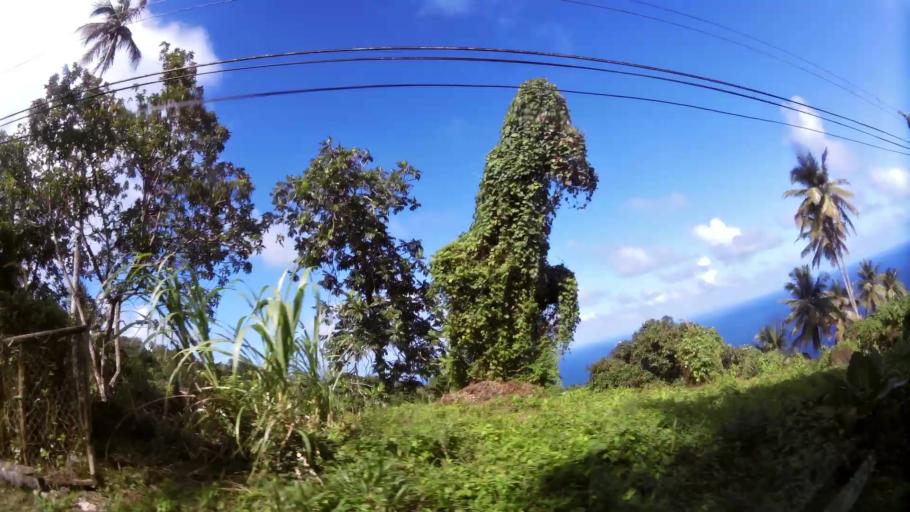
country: DM
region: Saint John
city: Portsmouth
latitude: 15.6258
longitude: -61.4185
